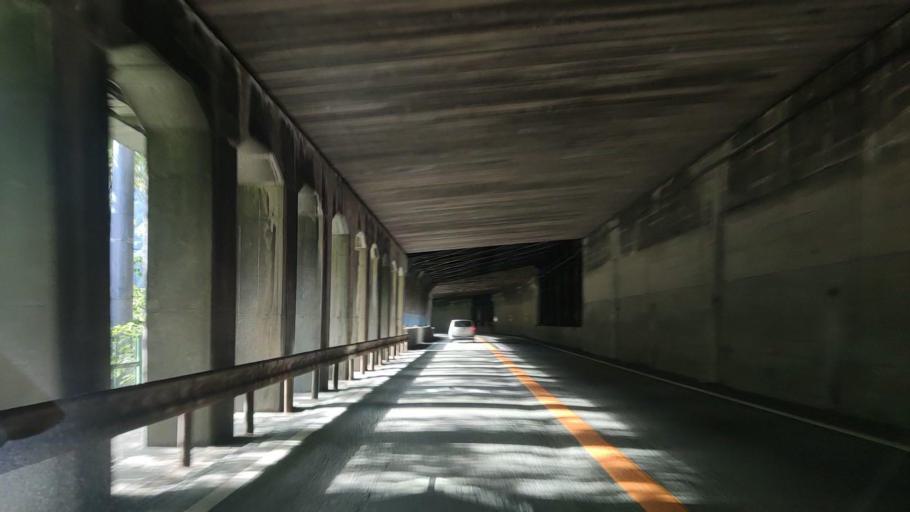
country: JP
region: Toyama
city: Yatsuomachi-higashikumisaka
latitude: 36.4457
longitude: 137.2733
